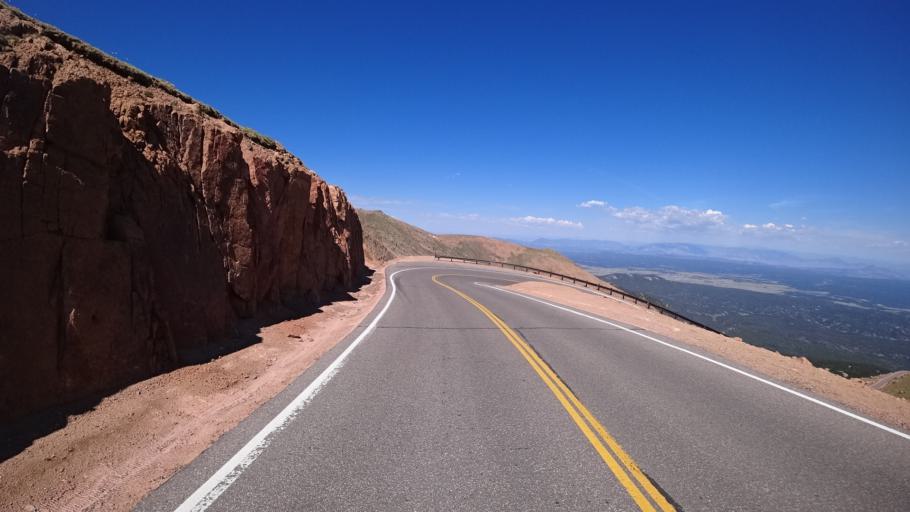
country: US
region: Colorado
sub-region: El Paso County
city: Cascade-Chipita Park
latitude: 38.8675
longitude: -105.0658
